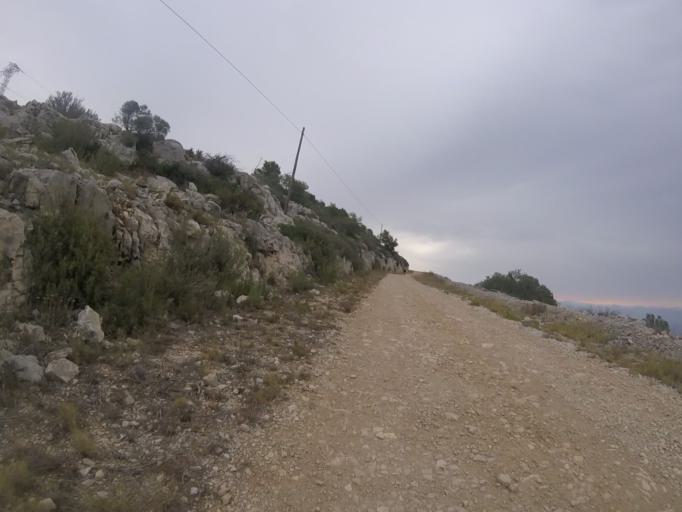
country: ES
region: Valencia
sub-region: Provincia de Castello
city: Alcoceber
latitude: 40.2746
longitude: 0.2791
